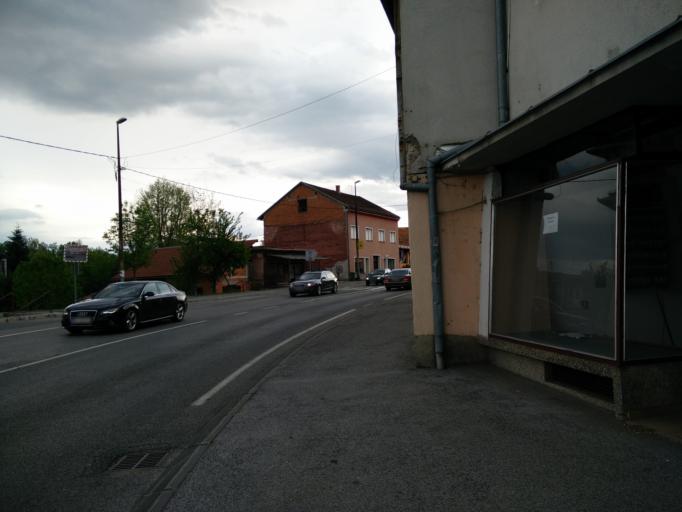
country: HR
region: Karlovacka
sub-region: Grad Karlovac
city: Slunj
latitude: 45.1162
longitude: 15.5861
